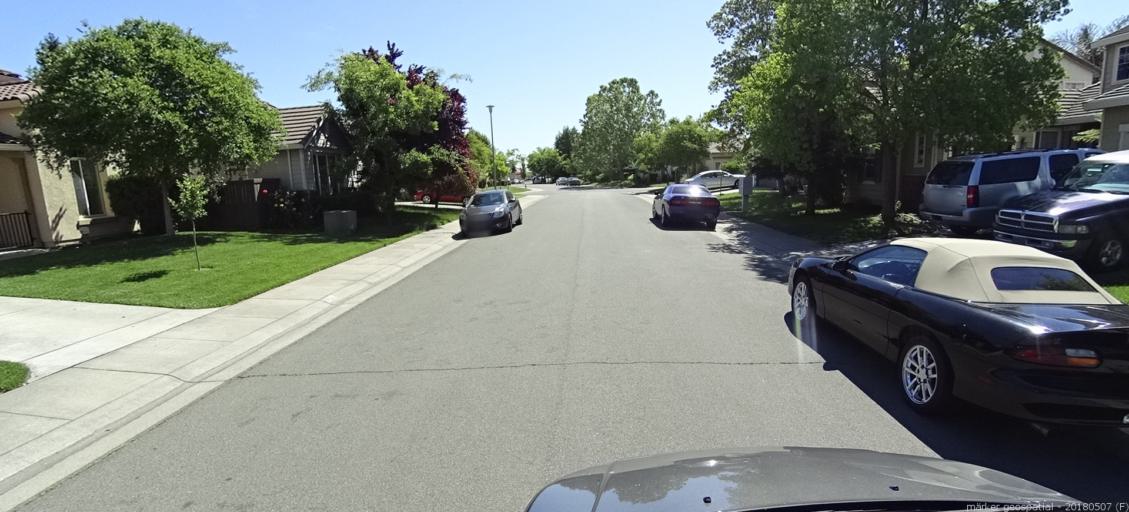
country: US
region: California
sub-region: Sacramento County
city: Rio Linda
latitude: 38.6582
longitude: -121.4980
